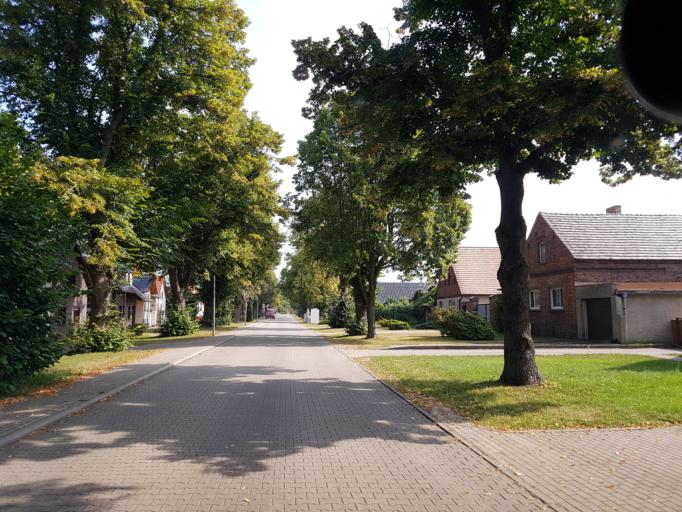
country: DE
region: Brandenburg
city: Finsterwalde
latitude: 51.6899
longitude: 13.7173
